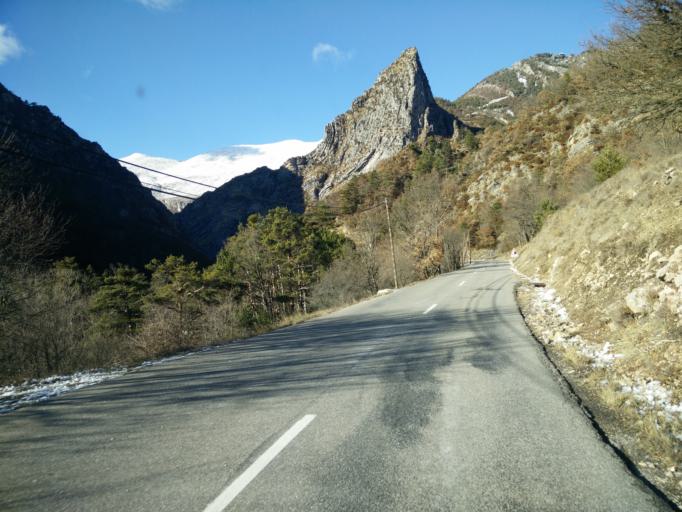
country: FR
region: Provence-Alpes-Cote d'Azur
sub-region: Departement des Alpes-de-Haute-Provence
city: Castellane
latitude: 43.8297
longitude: 6.4575
